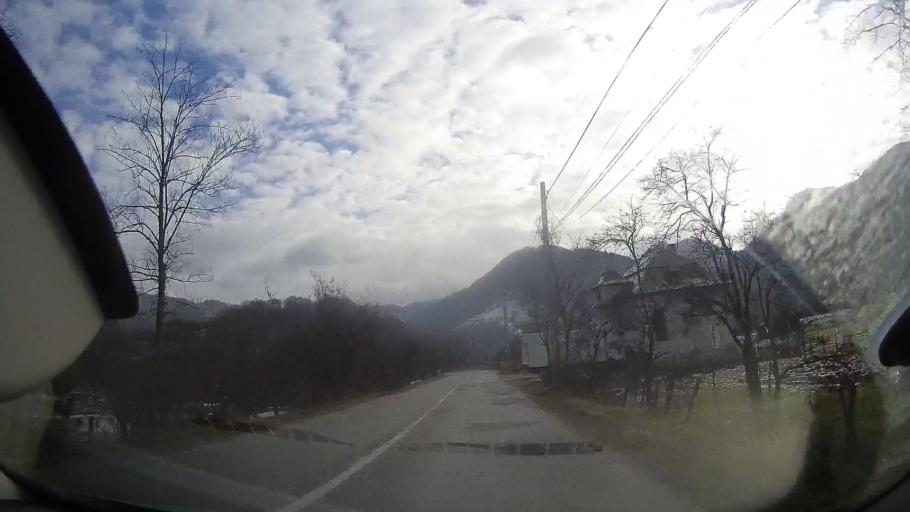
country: RO
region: Alba
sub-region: Comuna Lupsa
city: Lupsa
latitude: 46.3810
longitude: 23.2286
